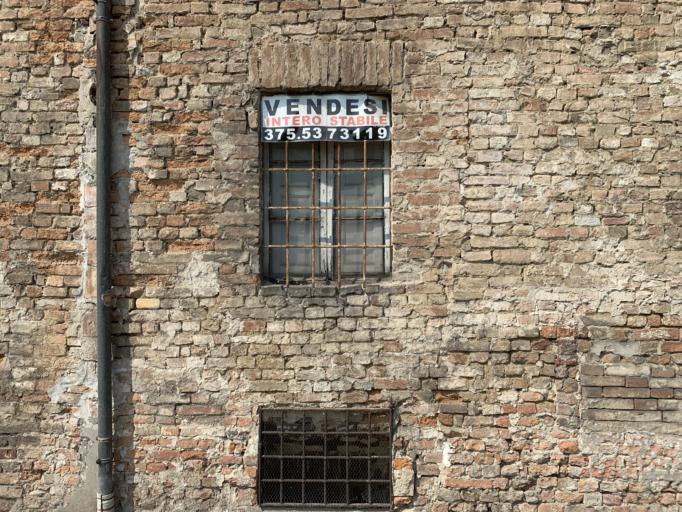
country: IT
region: Emilia-Romagna
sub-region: Provincia di Piacenza
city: Piacenza
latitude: 45.0466
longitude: 9.6999
